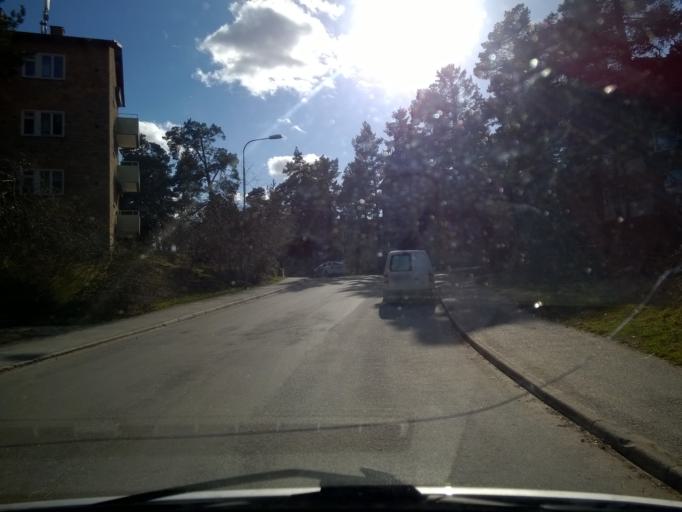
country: SE
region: Stockholm
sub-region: Stockholms Kommun
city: Bromma
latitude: 59.3317
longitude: 17.9479
